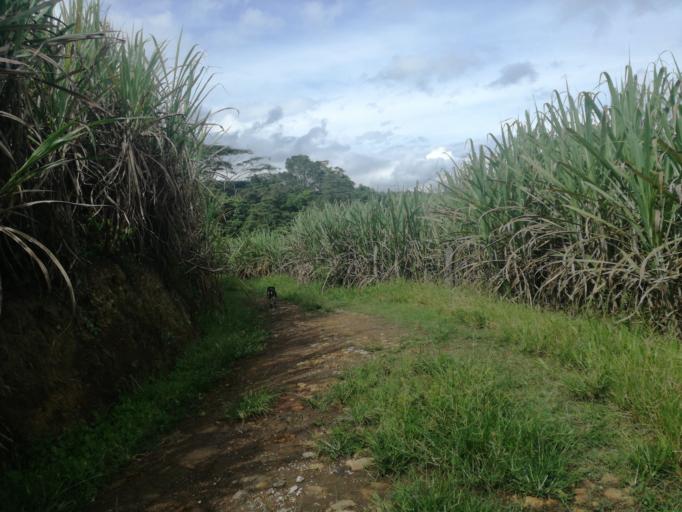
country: CO
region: Boyaca
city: Santana
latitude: 6.0584
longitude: -73.4864
